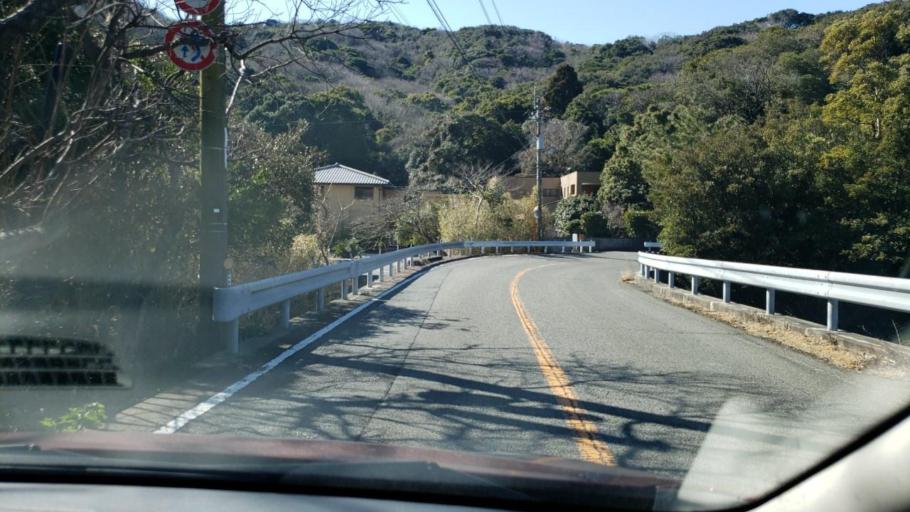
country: JP
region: Tokushima
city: Narutocho-mitsuishi
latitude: 34.2205
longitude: 134.5743
